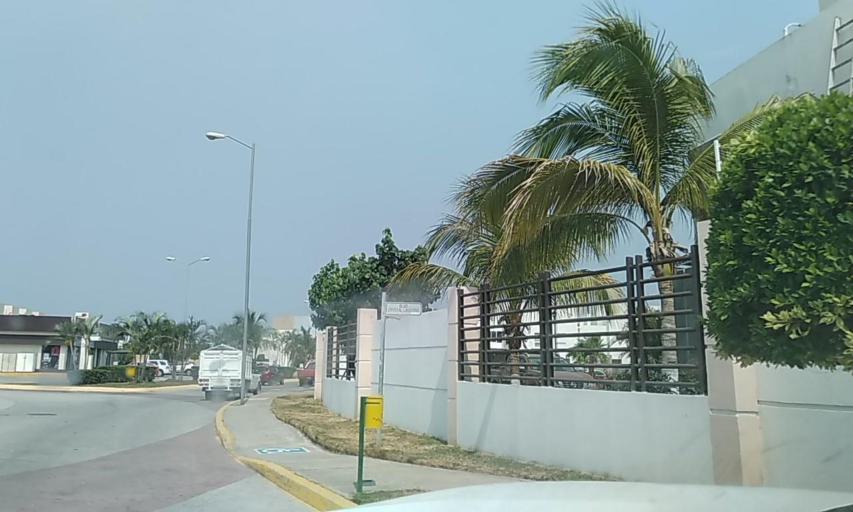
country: MX
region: Veracruz
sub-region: Veracruz
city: Hacienda Sotavento
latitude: 19.1330
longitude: -96.1722
